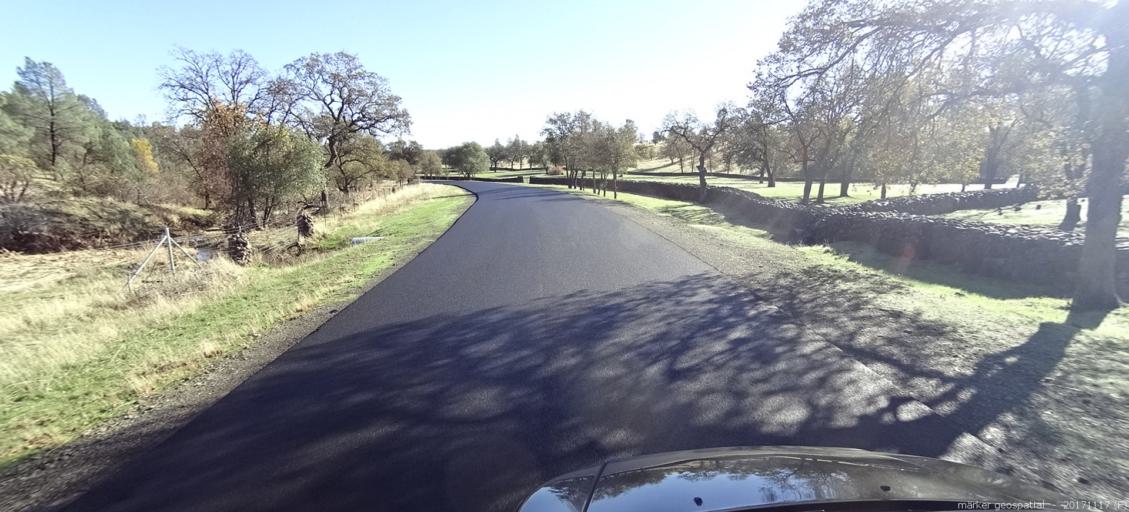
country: US
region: California
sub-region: Shasta County
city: Cottonwood
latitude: 40.4403
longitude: -122.1496
